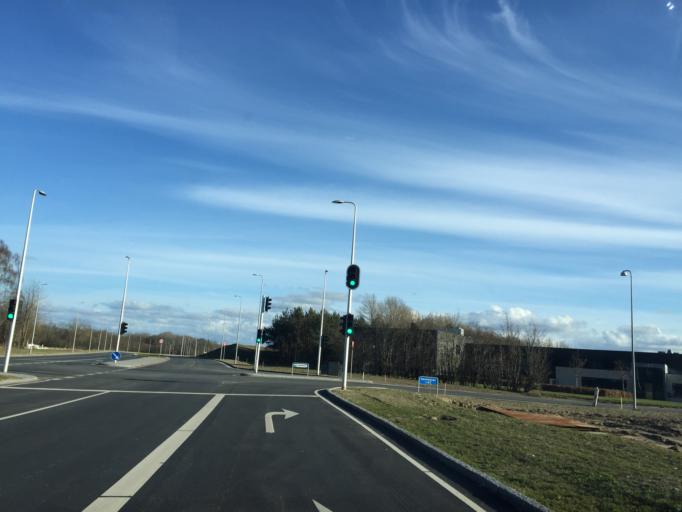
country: DK
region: South Denmark
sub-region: Odense Kommune
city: Hojby
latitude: 55.3573
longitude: 10.4163
